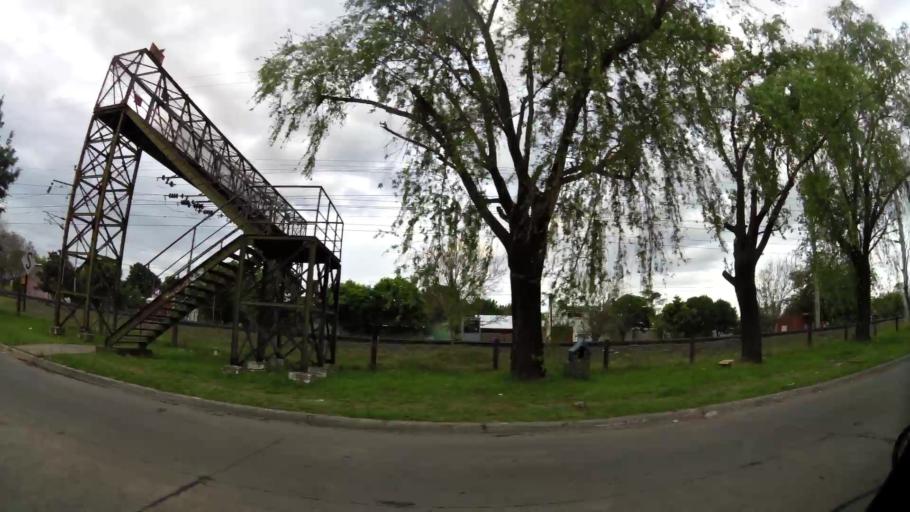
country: AR
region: Buenos Aires
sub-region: Partido de Quilmes
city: Quilmes
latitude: -34.7457
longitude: -58.2419
